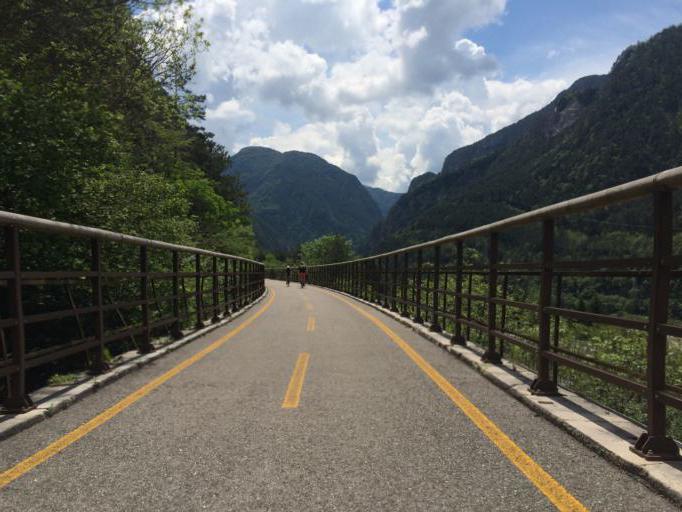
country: IT
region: Friuli Venezia Giulia
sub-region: Provincia di Udine
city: Dogna
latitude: 46.4386
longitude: 13.3115
